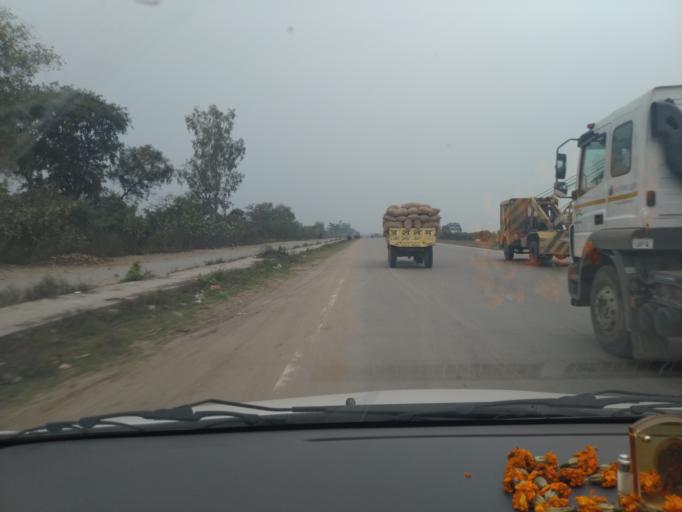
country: IN
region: Bihar
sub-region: Rohtas
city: Dehri
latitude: 24.9727
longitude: 83.9104
